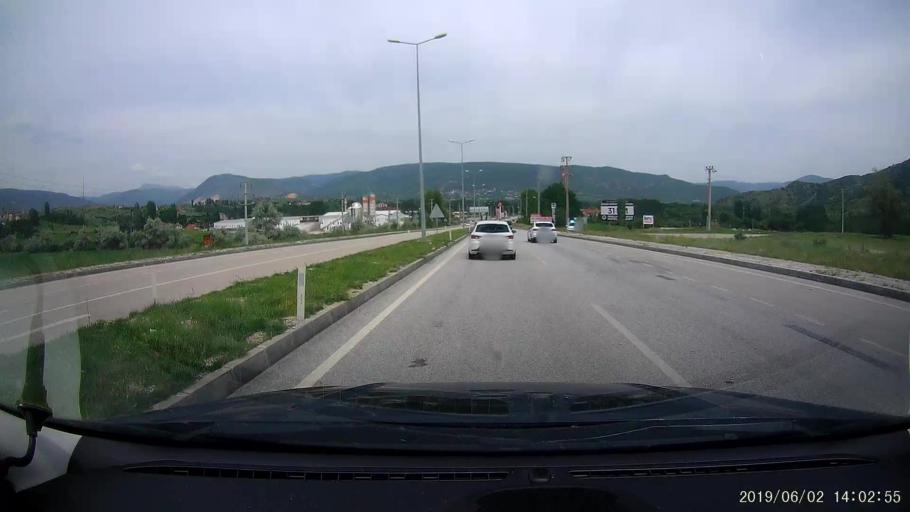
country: TR
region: Cankiri
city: Ilgaz
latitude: 40.9079
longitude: 33.6238
